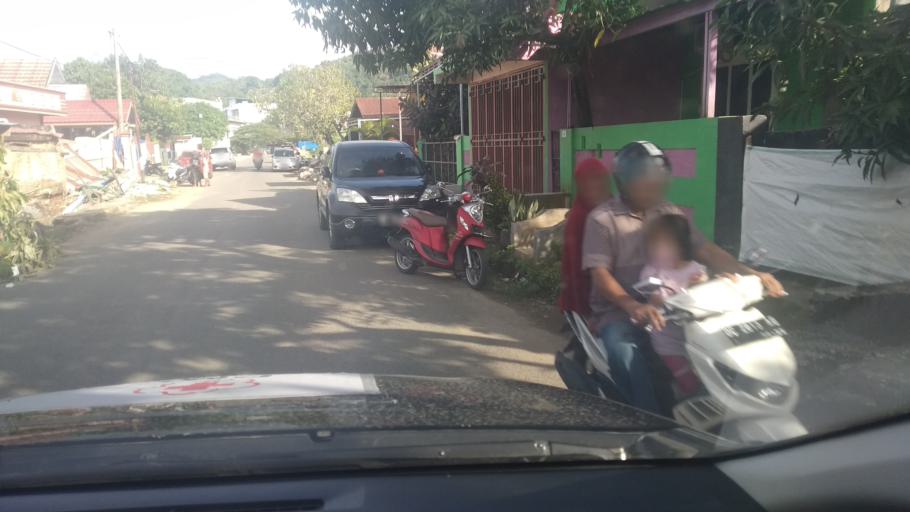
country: ID
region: Sulawesi Barat
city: Mamuju
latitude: -2.6808
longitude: 118.8869
